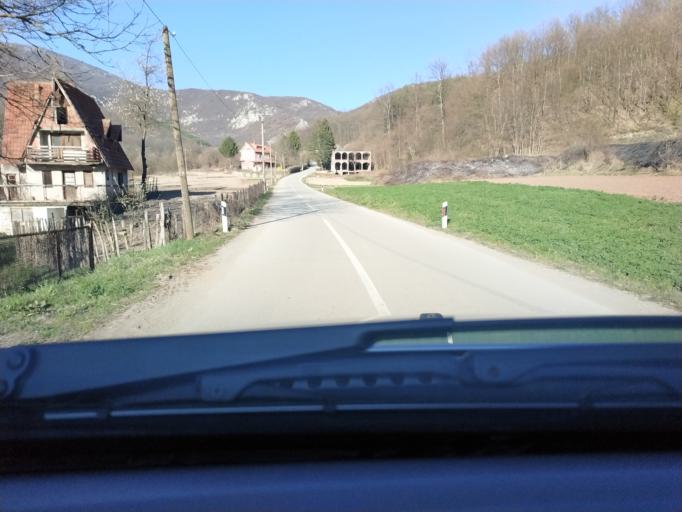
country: RS
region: Central Serbia
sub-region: Zajecarski Okrug
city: Soko Banja
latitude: 43.5558
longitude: 21.8245
